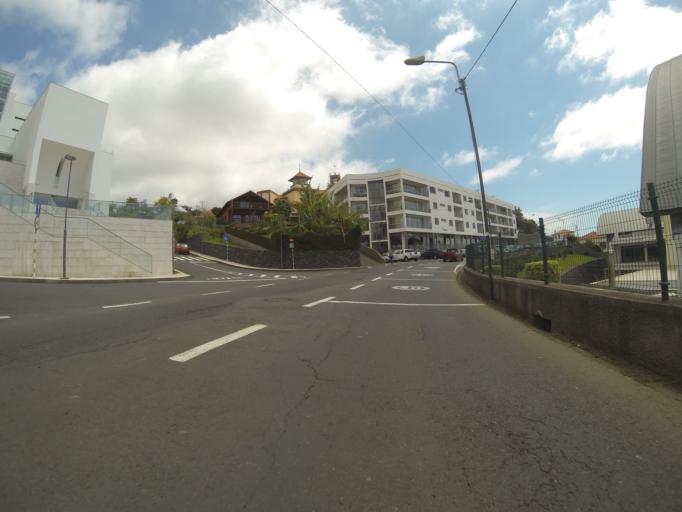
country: PT
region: Madeira
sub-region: Funchal
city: Nossa Senhora do Monte
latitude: 32.6656
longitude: -16.9334
